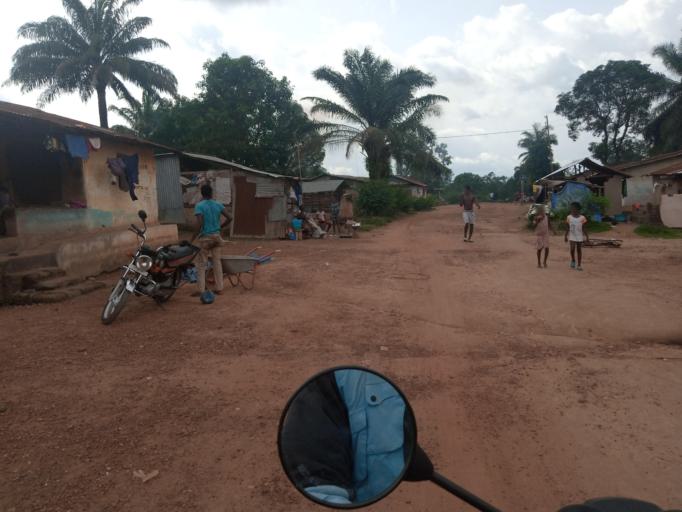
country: SL
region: Southern Province
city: Bo
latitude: 7.9867
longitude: -11.7428
